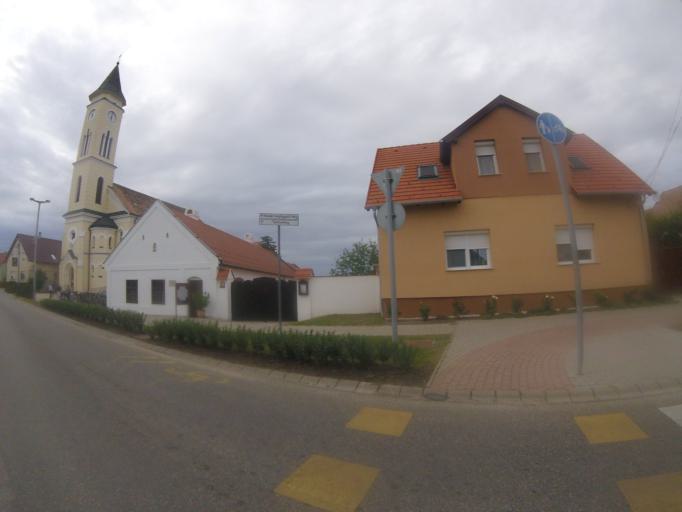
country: HU
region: Gyor-Moson-Sopron
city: Fertod
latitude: 47.6220
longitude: 16.7956
